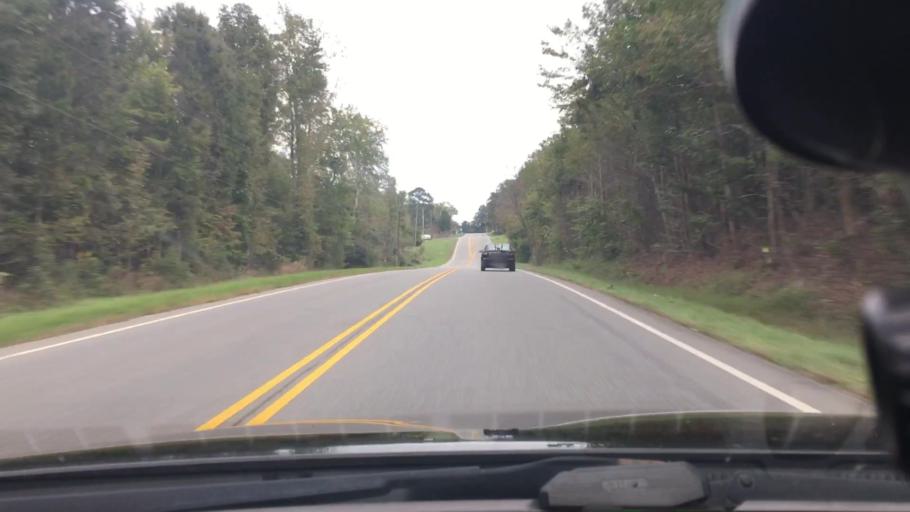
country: US
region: North Carolina
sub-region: Moore County
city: Robbins
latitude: 35.4045
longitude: -79.5811
